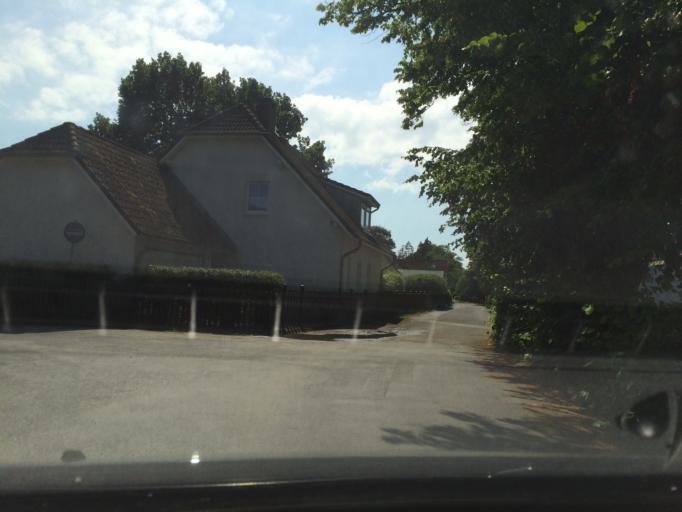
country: DE
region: Mecklenburg-Vorpommern
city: Ostseebad Prerow
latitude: 54.4428
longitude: 12.5777
